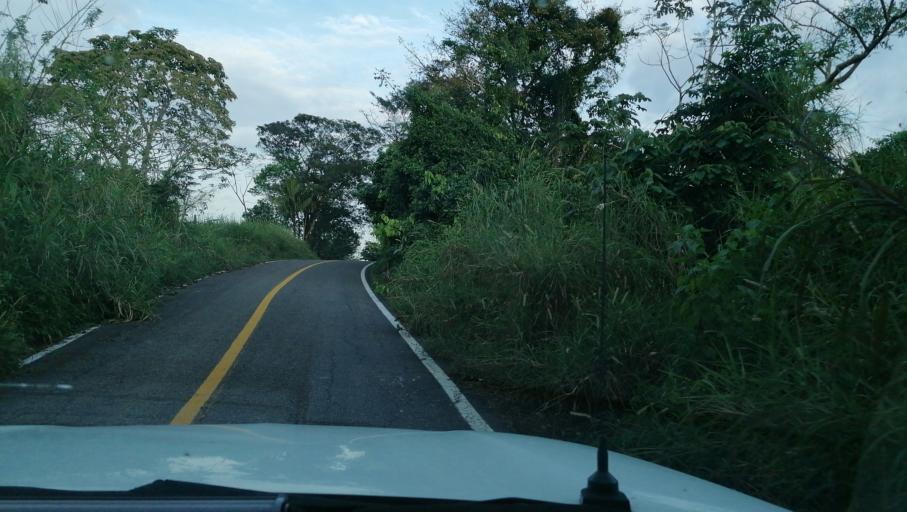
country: MX
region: Chiapas
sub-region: Juarez
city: El Triunfo 1ra. Seccion (Cardona)
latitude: 17.5057
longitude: -93.2255
